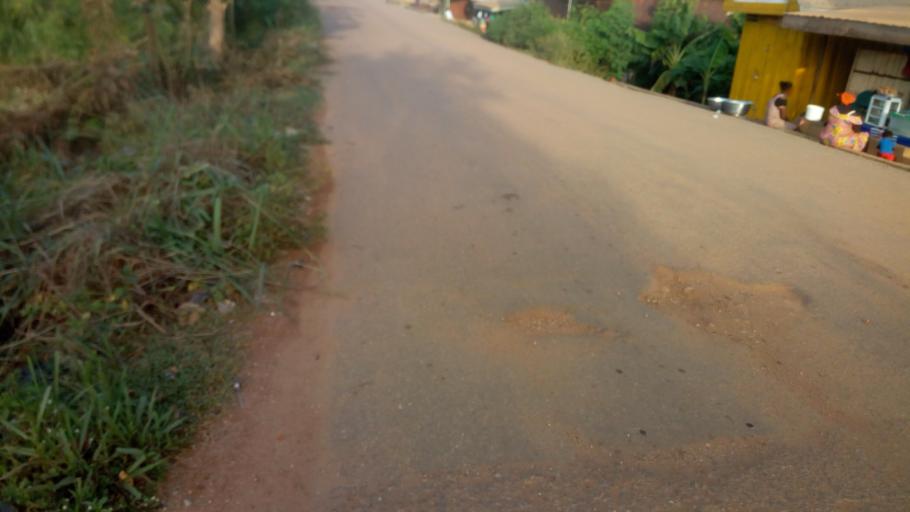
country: GH
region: Ashanti
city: Obuasi
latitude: 6.2130
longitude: -1.6969
